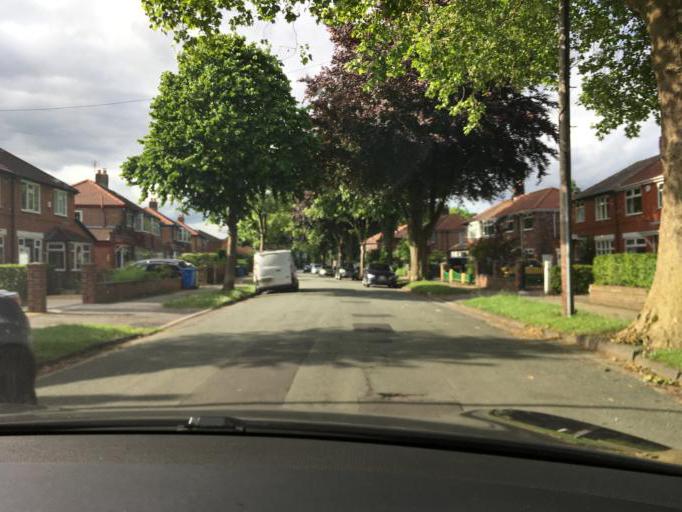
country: GB
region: England
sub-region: Trafford
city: Urmston
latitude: 53.4402
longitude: -2.3662
